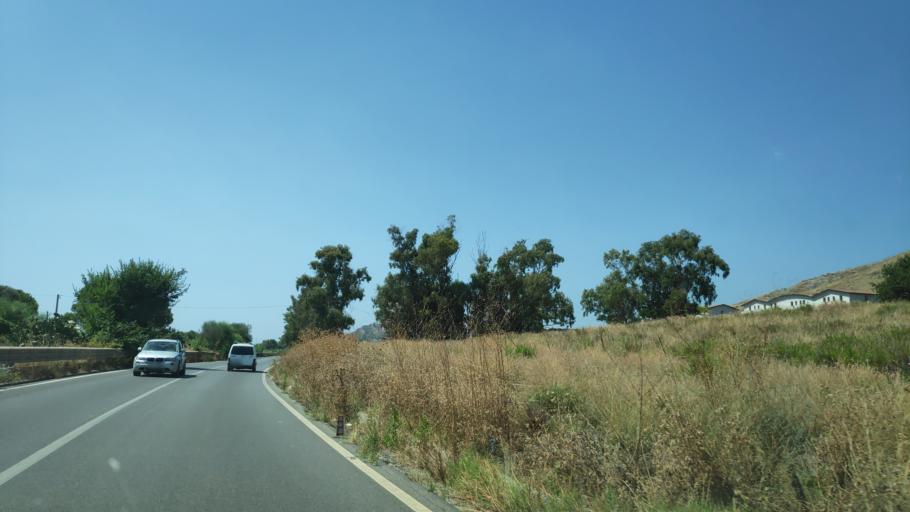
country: IT
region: Calabria
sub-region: Provincia di Reggio Calabria
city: Brancaleone-Marina
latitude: 37.9778
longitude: 16.1127
